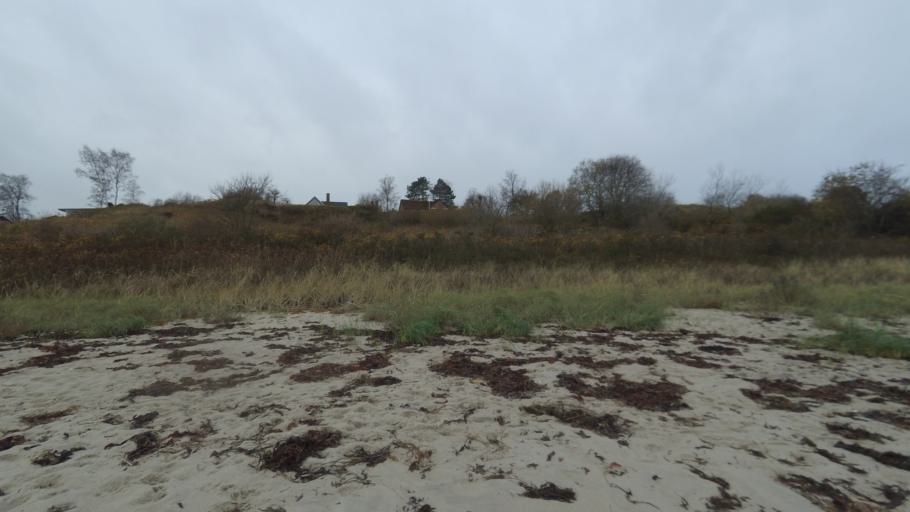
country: DK
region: Central Jutland
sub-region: Arhus Kommune
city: Malling
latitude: 55.9940
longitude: 10.2543
